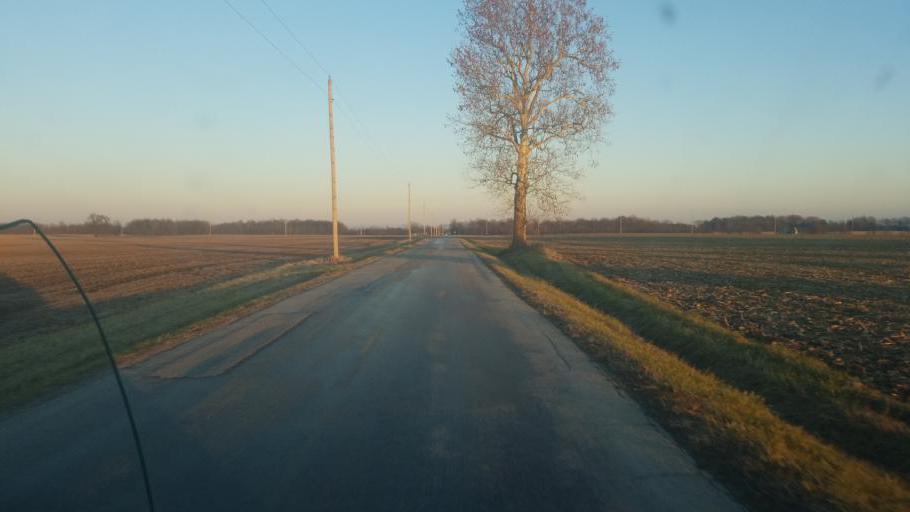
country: US
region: Ohio
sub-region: Union County
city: Richwood
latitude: 40.6219
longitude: -83.3310
